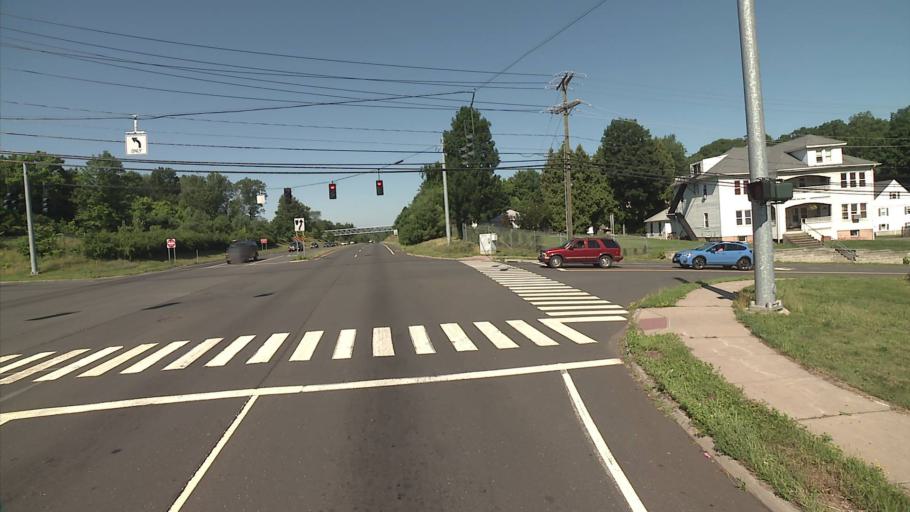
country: US
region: Connecticut
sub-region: Hartford County
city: Plainville
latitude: 41.6707
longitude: -72.8975
